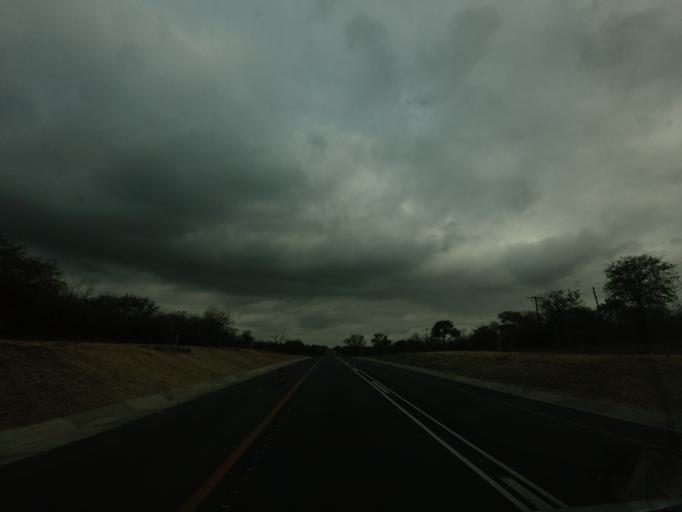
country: ZA
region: Mpumalanga
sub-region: Ehlanzeni District
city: Komatipoort
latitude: -25.4405
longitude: 31.7479
